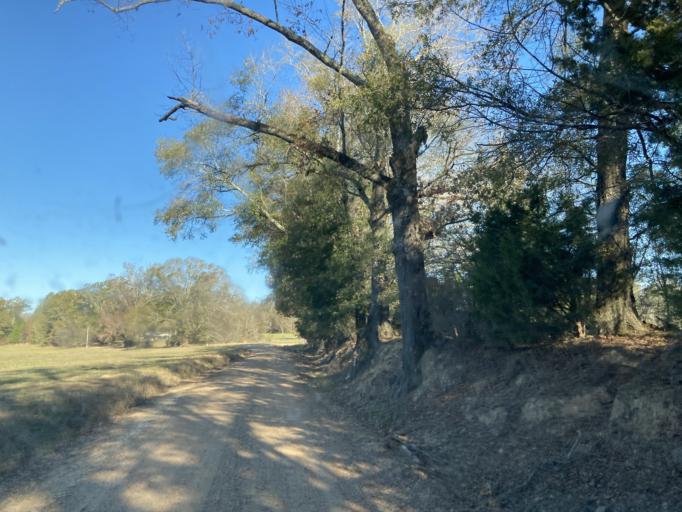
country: US
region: Mississippi
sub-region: Madison County
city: Kearney Park
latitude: 32.7248
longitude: -90.3075
